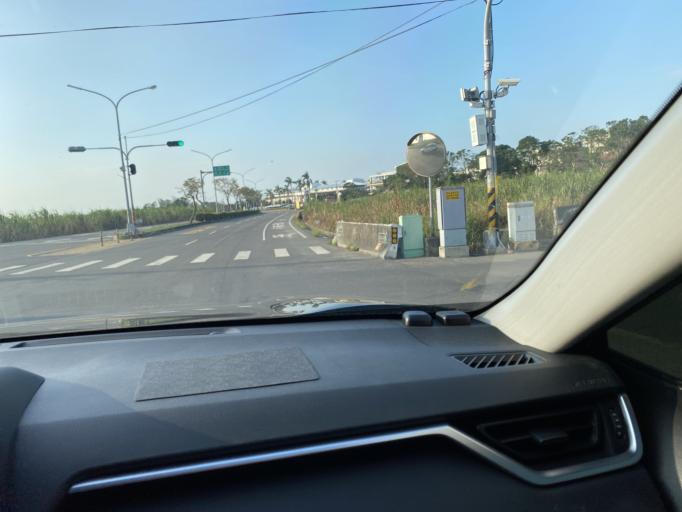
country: TW
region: Taiwan
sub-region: Changhua
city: Chang-hua
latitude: 23.9539
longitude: 120.4168
